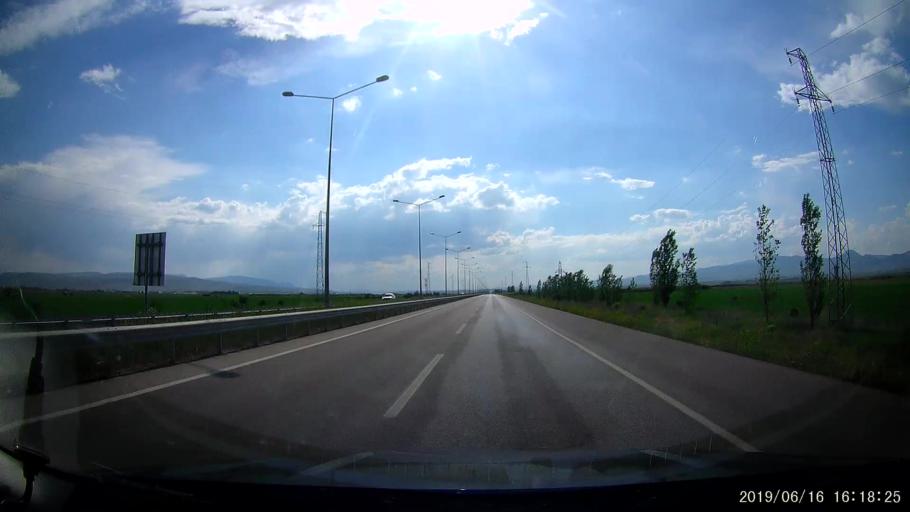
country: TR
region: Erzurum
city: Ilica
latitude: 39.9646
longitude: 41.1676
